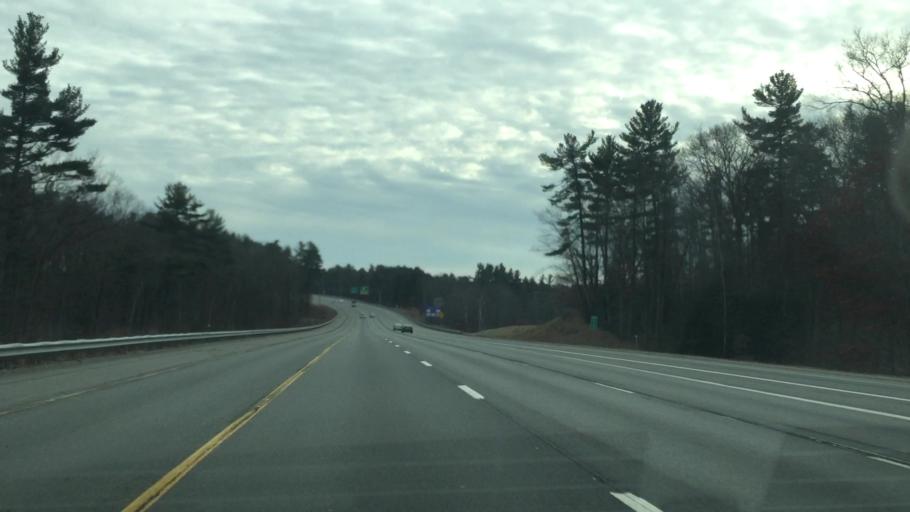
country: US
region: New Hampshire
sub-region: Rockingham County
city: Windham
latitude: 42.8209
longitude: -71.2887
